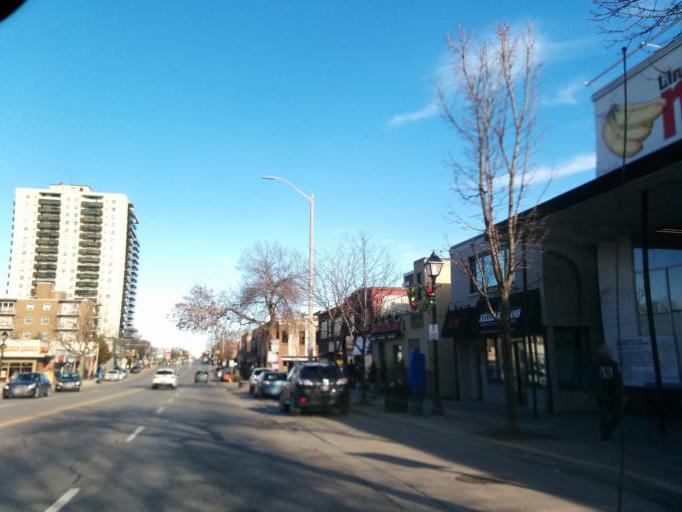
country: CA
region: Ontario
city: Mississauga
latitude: 43.5533
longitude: -79.5835
